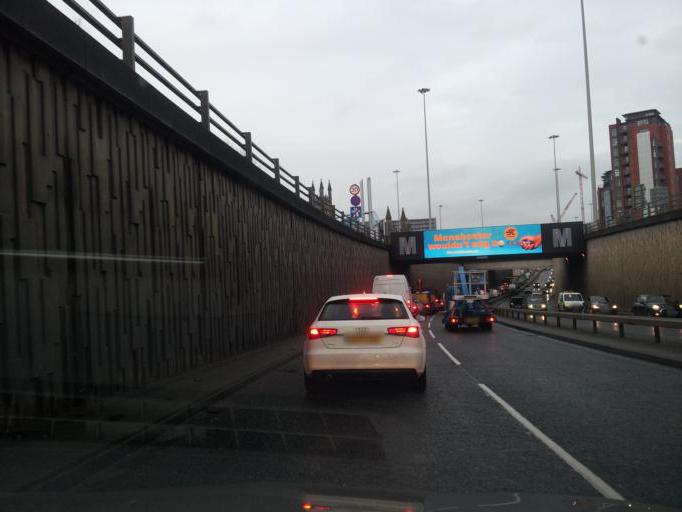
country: GB
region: England
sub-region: Manchester
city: Hulme
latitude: 53.4712
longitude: -2.2559
